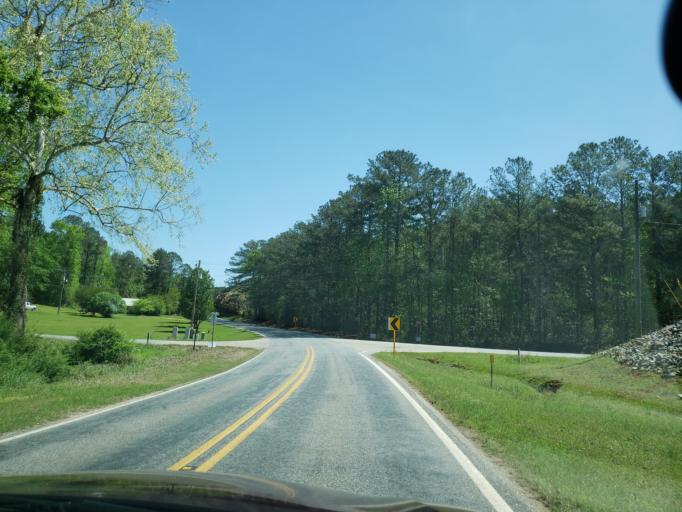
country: US
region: Alabama
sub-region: Tallapoosa County
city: Dadeville
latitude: 32.6984
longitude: -85.8476
